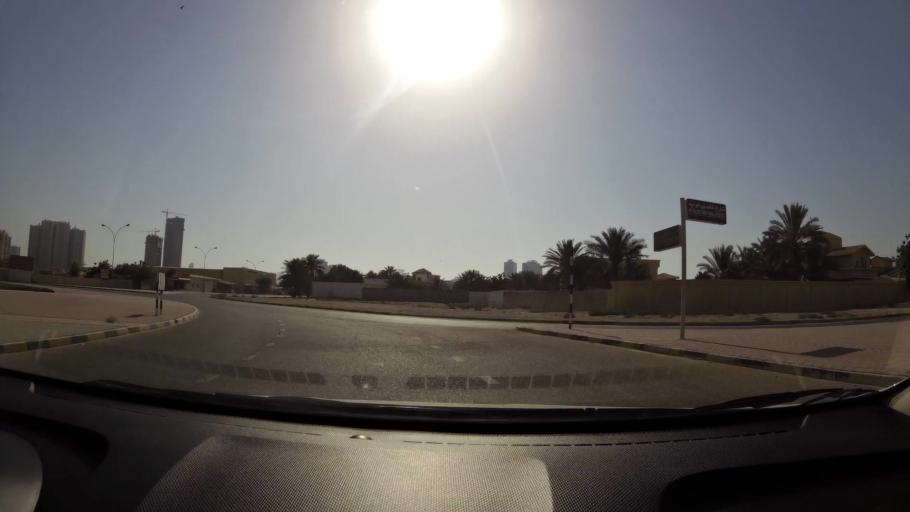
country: AE
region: Ajman
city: Ajman
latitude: 25.4001
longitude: 55.4625
